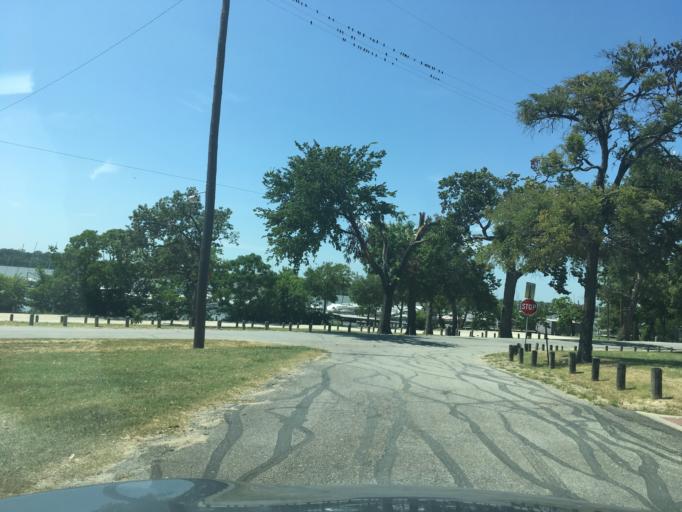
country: US
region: Texas
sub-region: Dallas County
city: Highland Park
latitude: 32.8431
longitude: -96.7182
